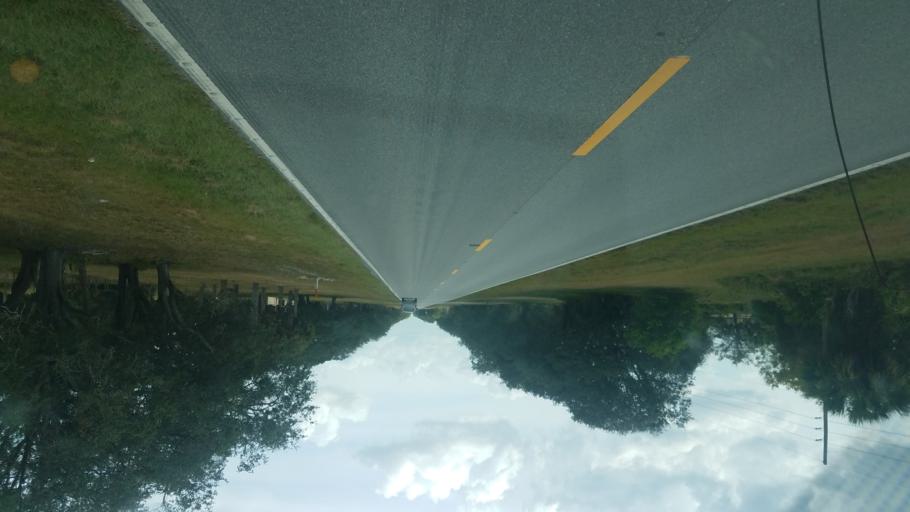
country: US
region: Florida
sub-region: Okeechobee County
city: Cypress Quarters
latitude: 27.4500
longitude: -80.7021
